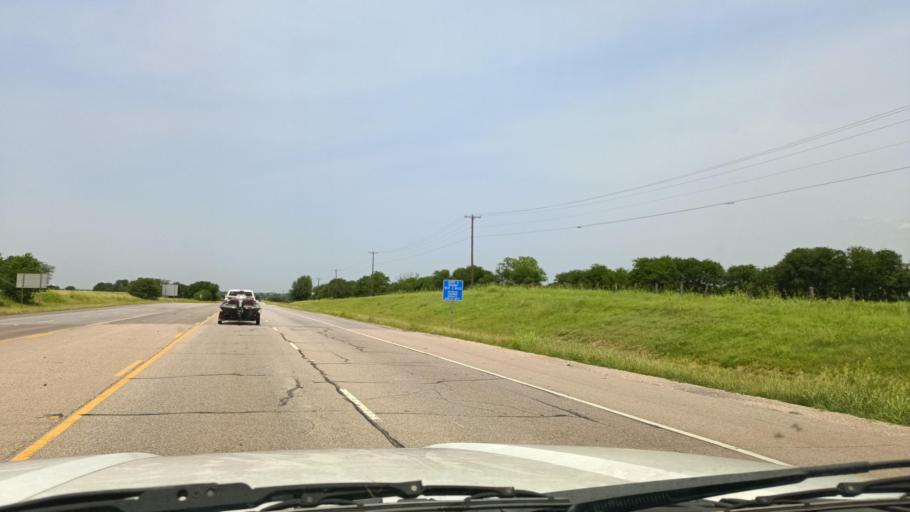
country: US
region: Texas
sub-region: Bell County
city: Temple
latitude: 31.1217
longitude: -97.3885
